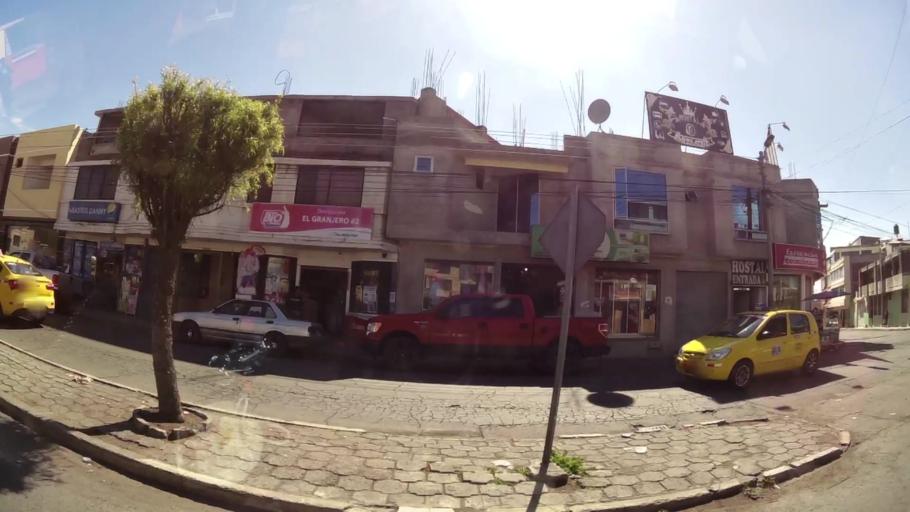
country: EC
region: Chimborazo
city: Riobamba
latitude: -1.6642
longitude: -78.6495
